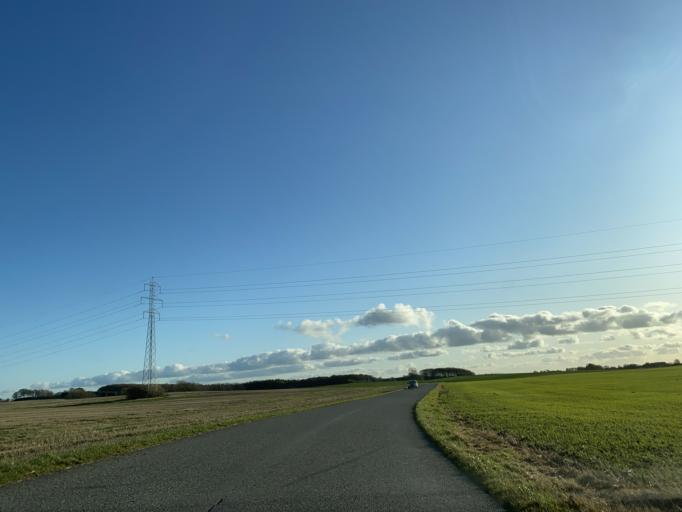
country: DK
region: Central Jutland
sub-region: Viborg Kommune
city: Bjerringbro
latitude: 56.3499
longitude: 9.7182
